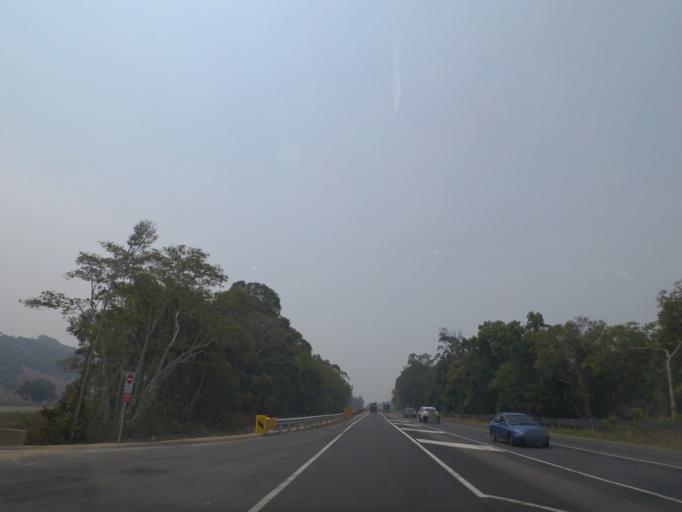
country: AU
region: New South Wales
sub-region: Ballina
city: Ballina
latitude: -28.9191
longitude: 153.4766
